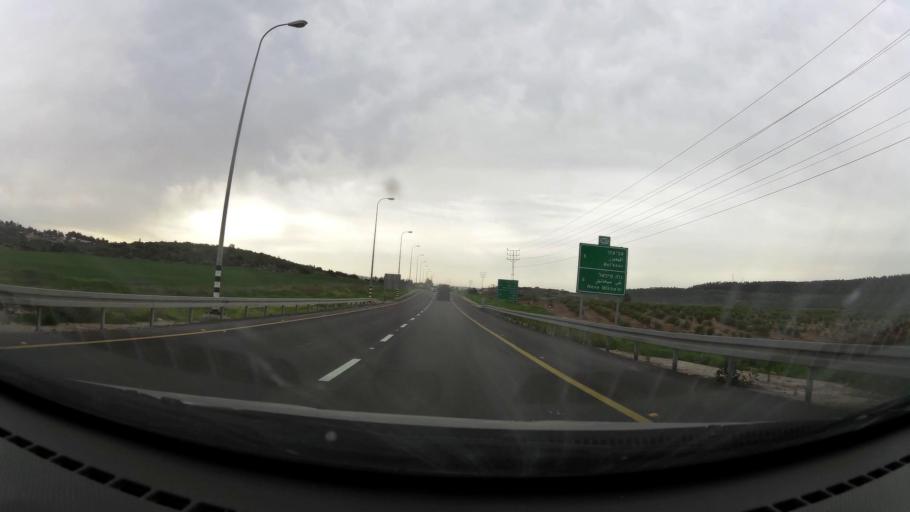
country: IL
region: Jerusalem
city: Bet Shemesh
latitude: 31.6795
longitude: 35.0041
